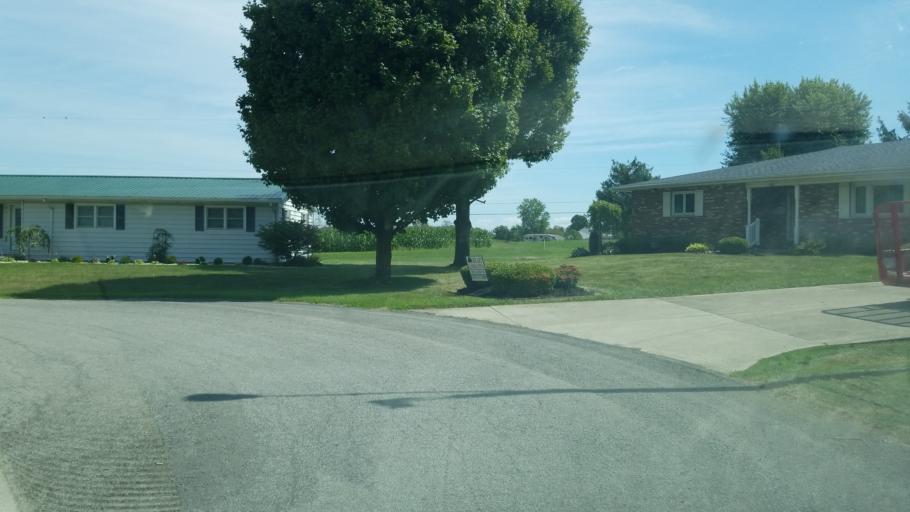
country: US
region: Ohio
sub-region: Hardin County
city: Kenton
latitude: 40.6604
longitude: -83.6006
